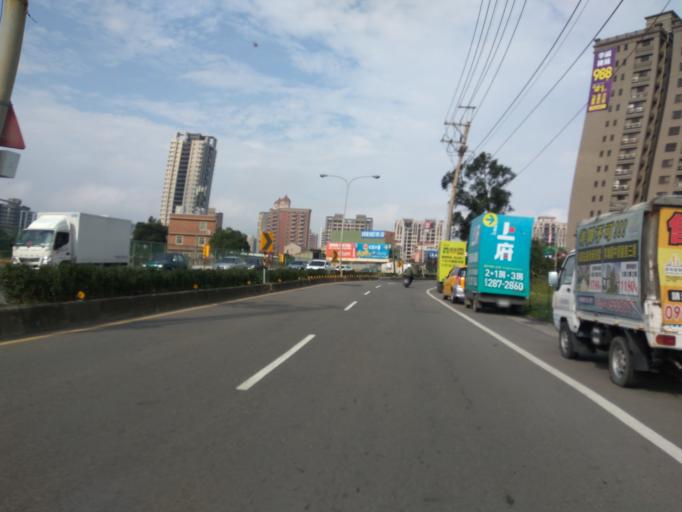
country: TW
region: Taiwan
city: Taoyuan City
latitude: 25.0026
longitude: 121.2150
